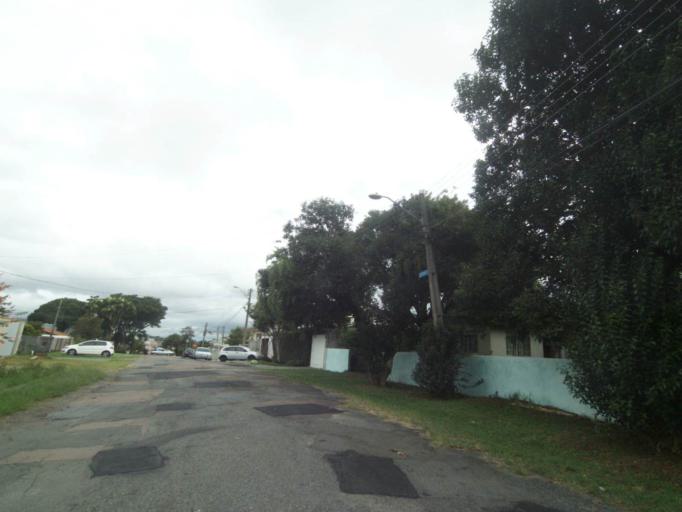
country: BR
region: Parana
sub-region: Curitiba
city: Curitiba
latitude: -25.4837
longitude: -49.2843
